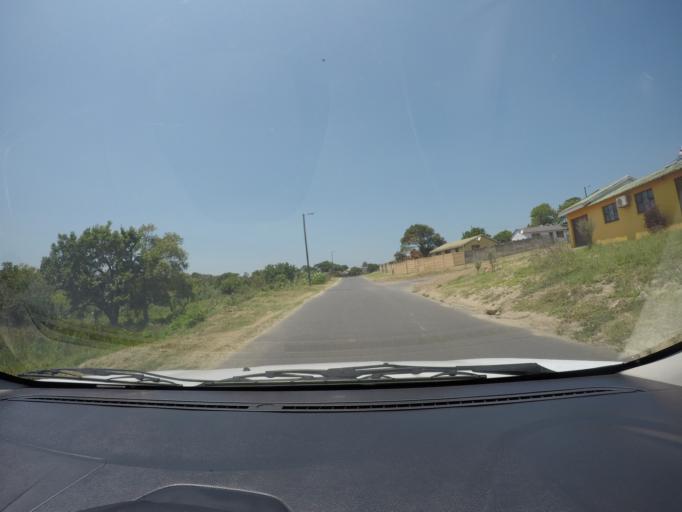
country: ZA
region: KwaZulu-Natal
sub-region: uThungulu District Municipality
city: eSikhawini
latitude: -28.8736
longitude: 31.9103
